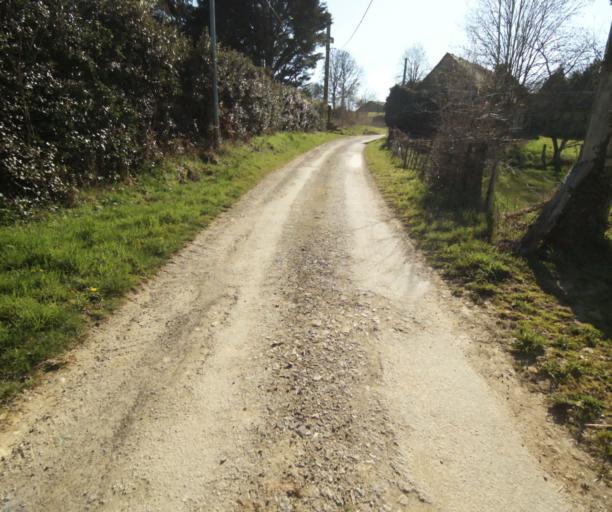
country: FR
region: Limousin
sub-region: Departement de la Correze
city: Chamboulive
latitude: 45.4734
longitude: 1.6868
